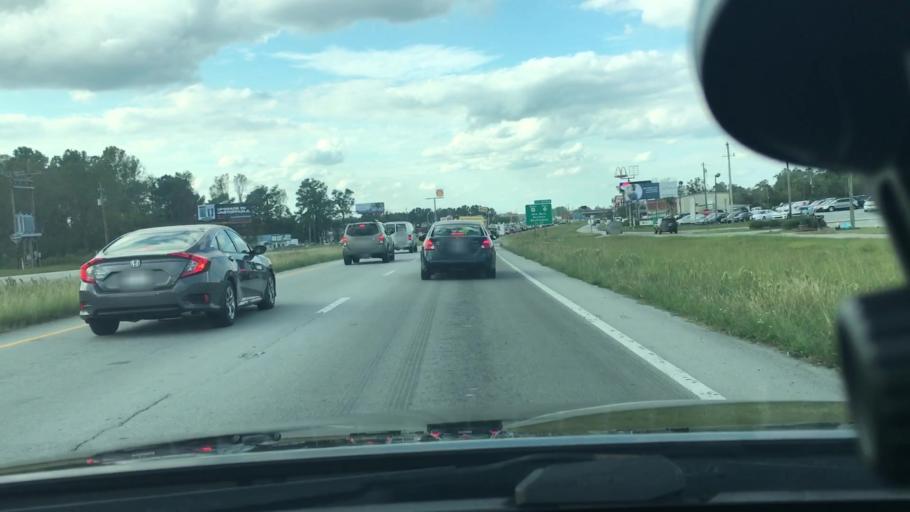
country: US
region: North Carolina
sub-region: Craven County
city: James City
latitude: 35.0778
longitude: -77.0295
